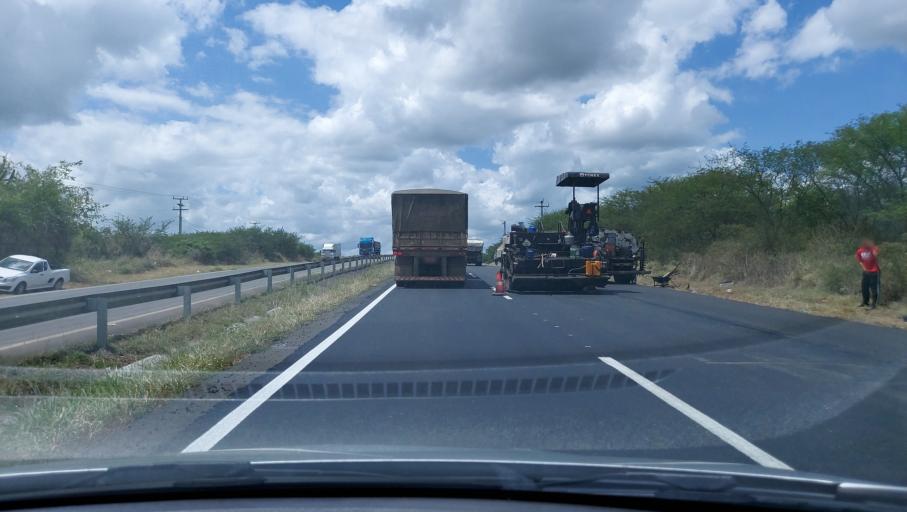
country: BR
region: Bahia
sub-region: Santo Estevao
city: Santo Estevao
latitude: -12.4245
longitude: -39.2050
